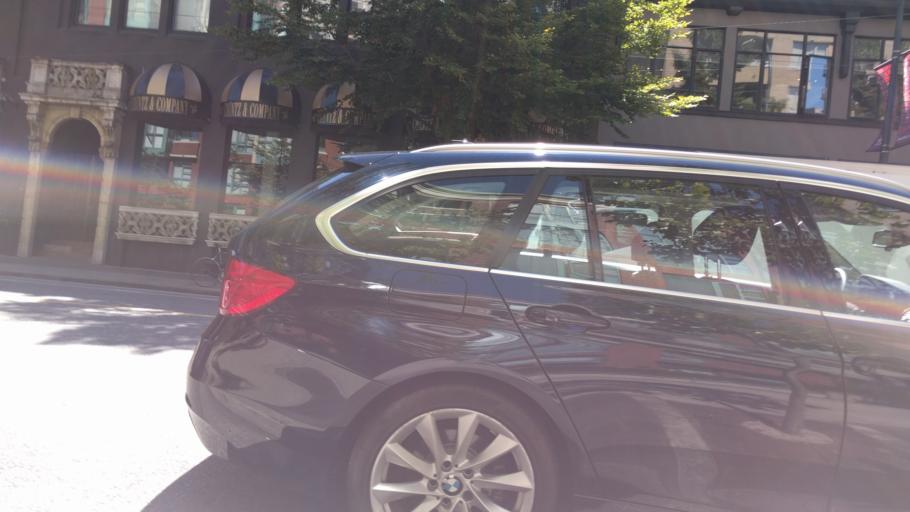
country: CA
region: British Columbia
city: West End
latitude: 49.2776
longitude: -123.1200
